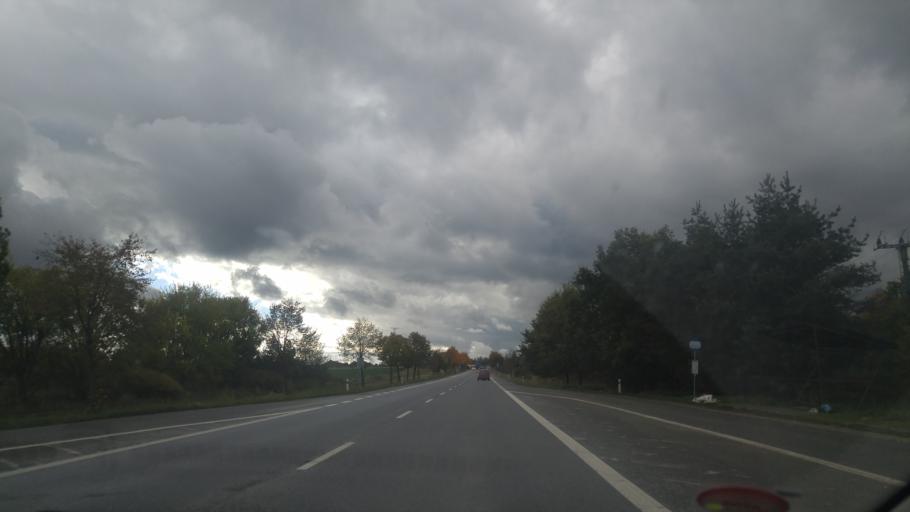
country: CZ
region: Jihocesky
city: Sevetin
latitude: 49.1183
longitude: 14.5898
